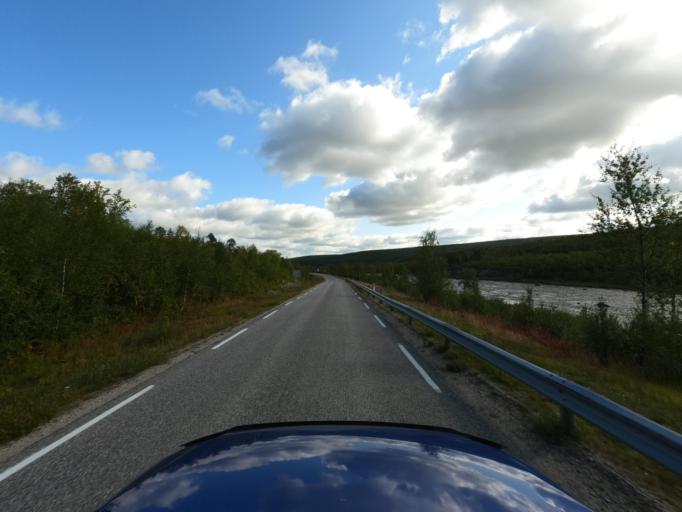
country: NO
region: Finnmark Fylke
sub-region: Porsanger
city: Lakselv
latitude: 69.4221
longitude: 24.8174
